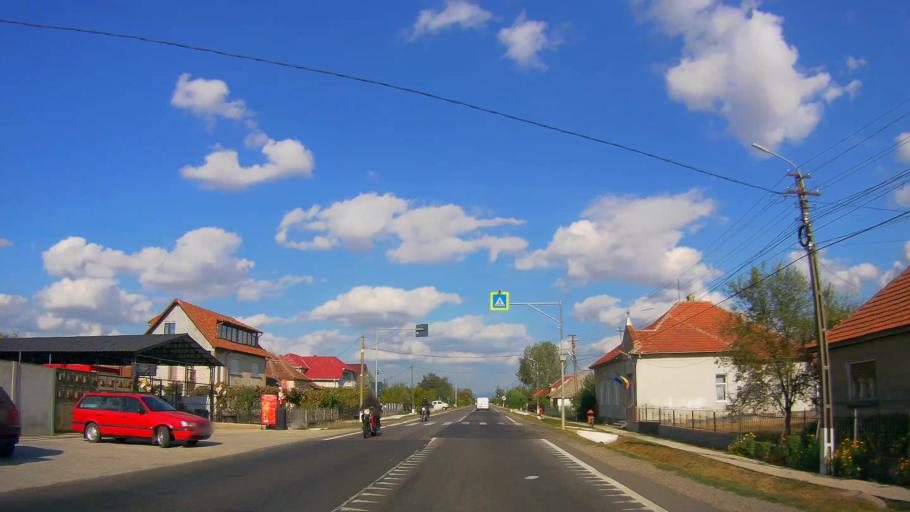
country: RO
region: Satu Mare
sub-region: Comuna Agris
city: Agris
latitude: 47.8665
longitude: 23.0021
